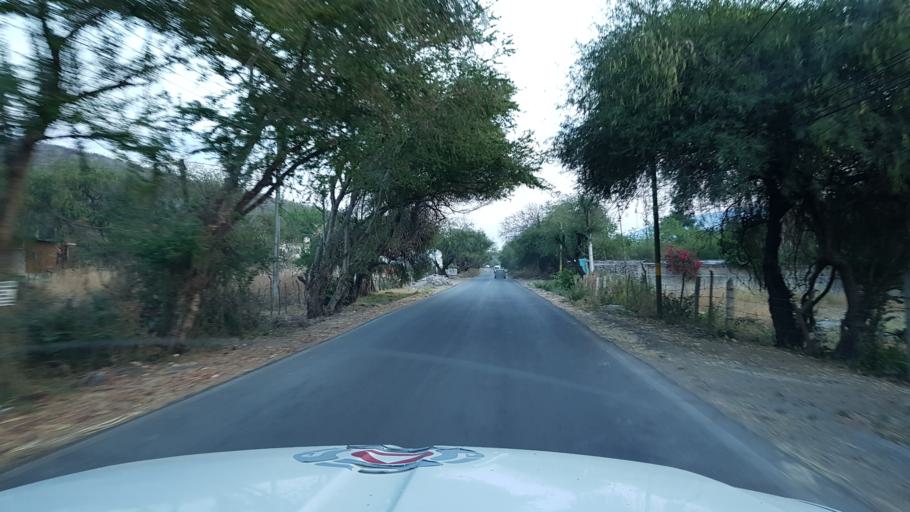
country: MX
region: Morelos
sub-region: Tlaltizapan de Zapata
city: Colonia Palo Prieto (Chipitongo)
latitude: 18.7096
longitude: -99.1075
